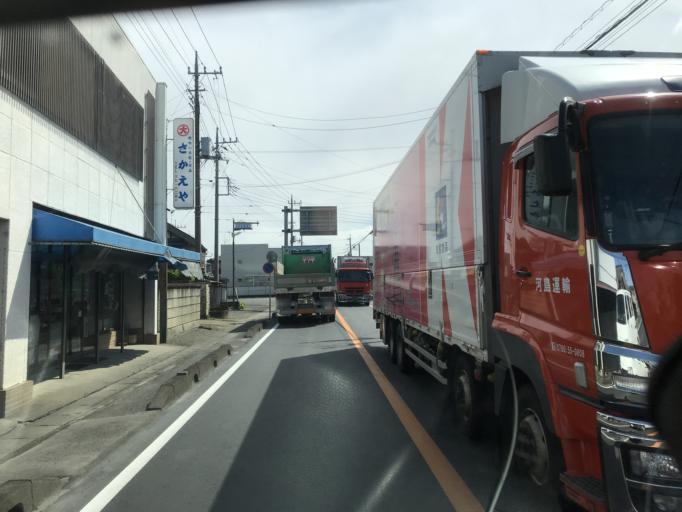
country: JP
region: Ibaraki
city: Yuki
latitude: 36.2511
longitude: 139.9152
